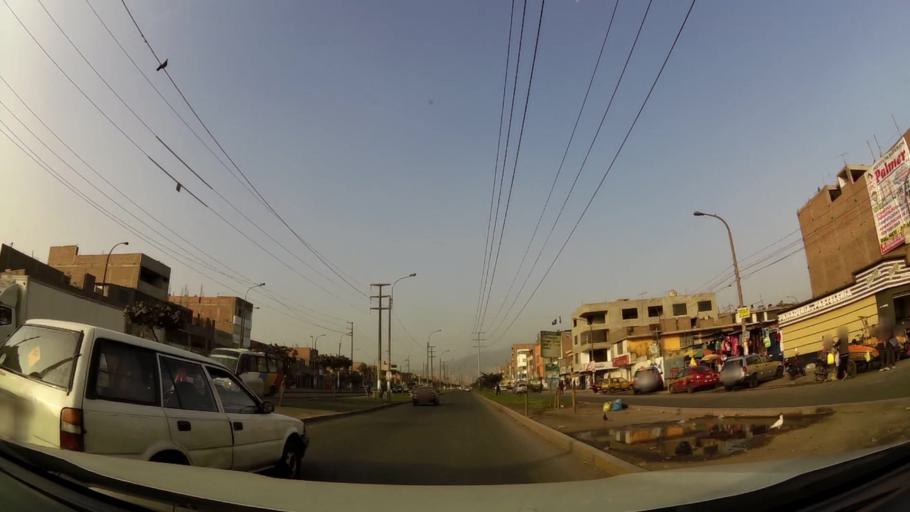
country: PE
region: Lima
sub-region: Lima
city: Independencia
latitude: -11.9487
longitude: -77.0802
